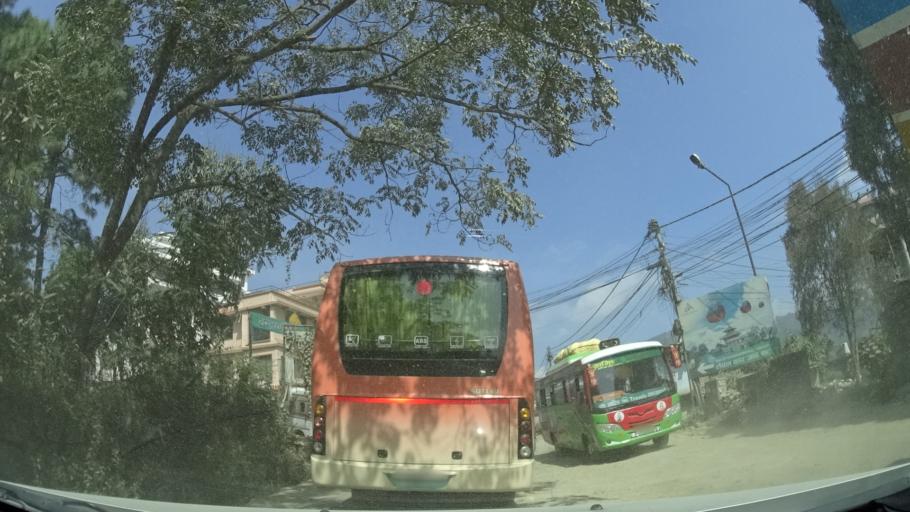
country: NP
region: Central Region
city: Kirtipur
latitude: 27.6911
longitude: 85.2208
